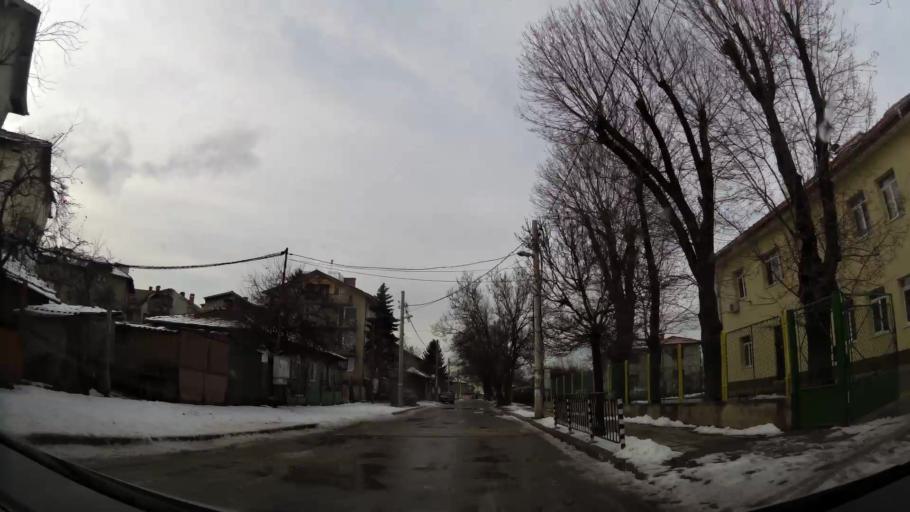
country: BG
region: Sofia-Capital
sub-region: Stolichna Obshtina
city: Sofia
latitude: 42.7183
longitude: 23.3469
